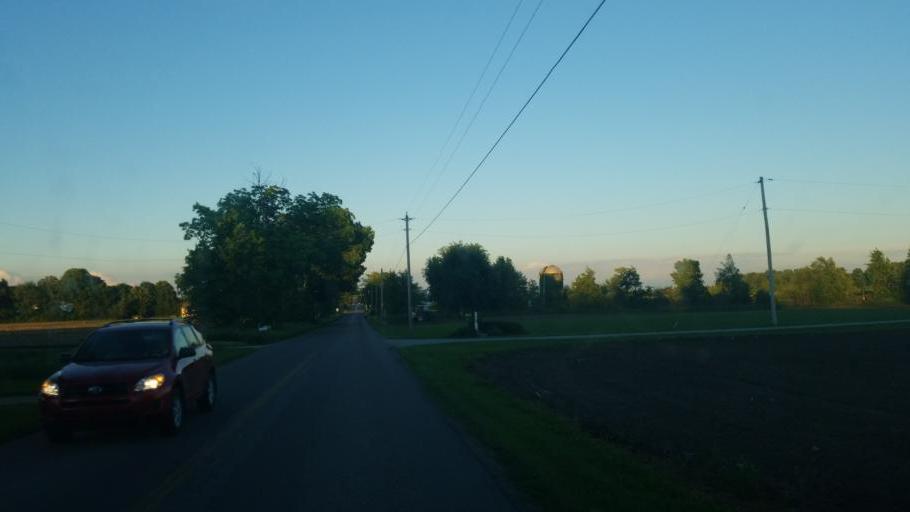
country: US
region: Indiana
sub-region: Elkhart County
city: Nappanee
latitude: 41.4265
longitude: -86.0246
